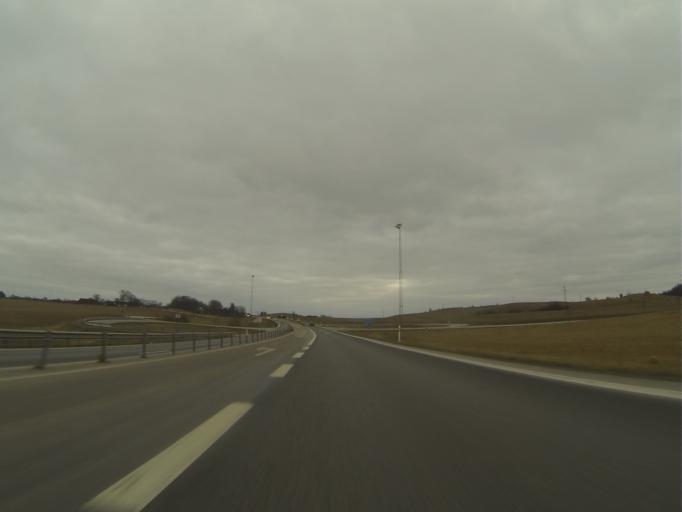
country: SE
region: Skane
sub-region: Trelleborgs Kommun
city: Anderslov
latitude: 55.5003
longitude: 13.3871
